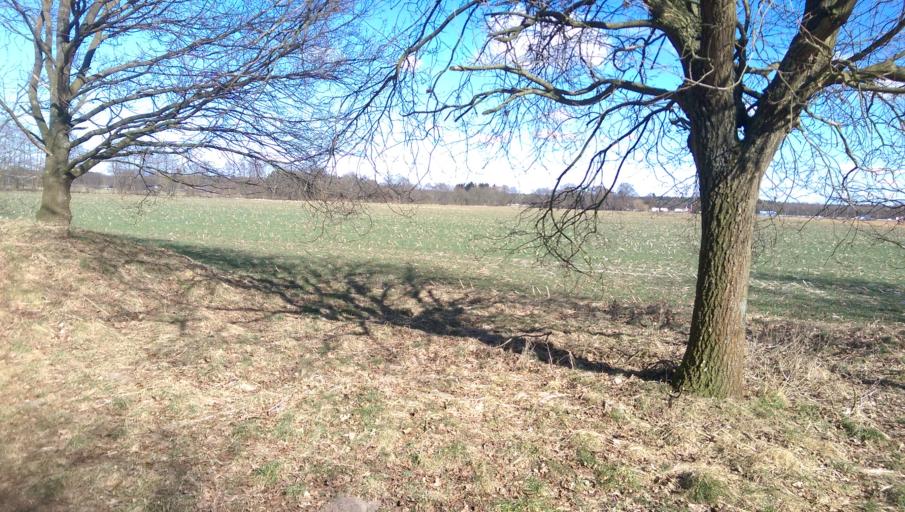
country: DE
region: Lower Saxony
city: Elze
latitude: 52.5459
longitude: 9.7864
